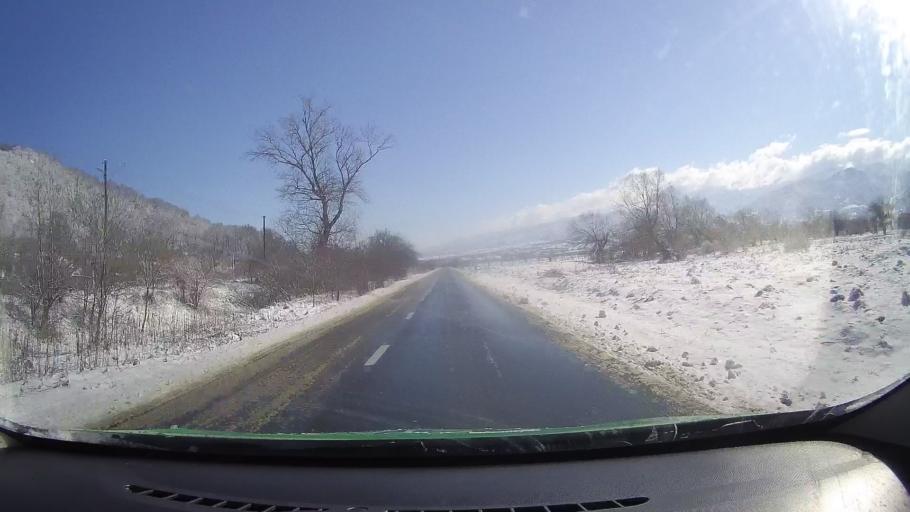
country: RO
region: Sibiu
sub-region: Comuna Talmaciu
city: Talmaciu
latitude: 45.6615
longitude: 24.2896
